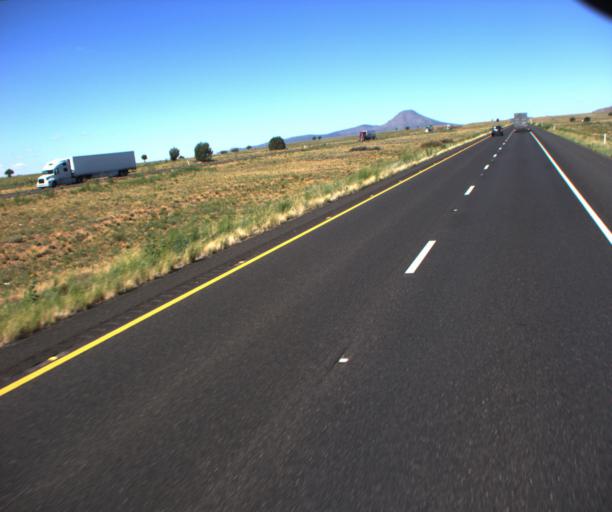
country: US
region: Arizona
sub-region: Yavapai County
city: Paulden
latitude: 35.2331
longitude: -112.6119
